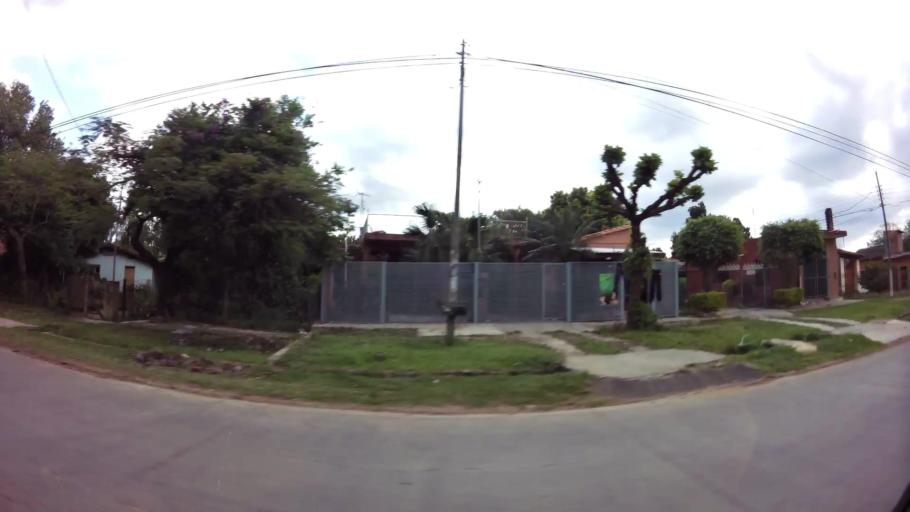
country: PY
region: Central
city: Fernando de la Mora
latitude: -25.2861
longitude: -57.5172
